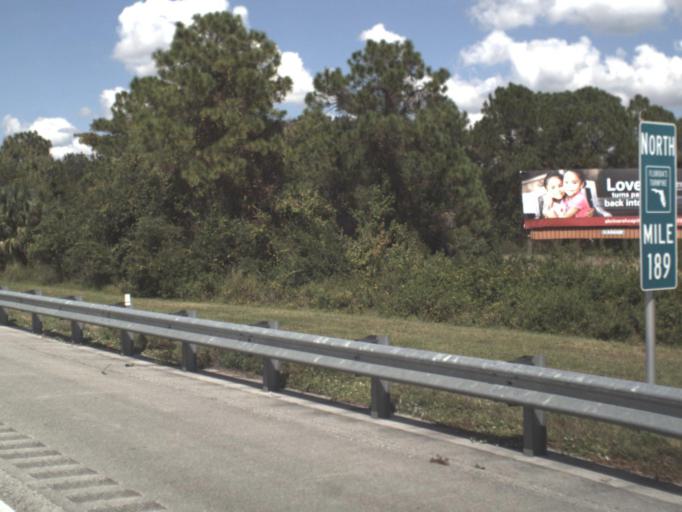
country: US
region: Florida
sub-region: Indian River County
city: Fellsmere
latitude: 27.6485
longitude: -80.8574
